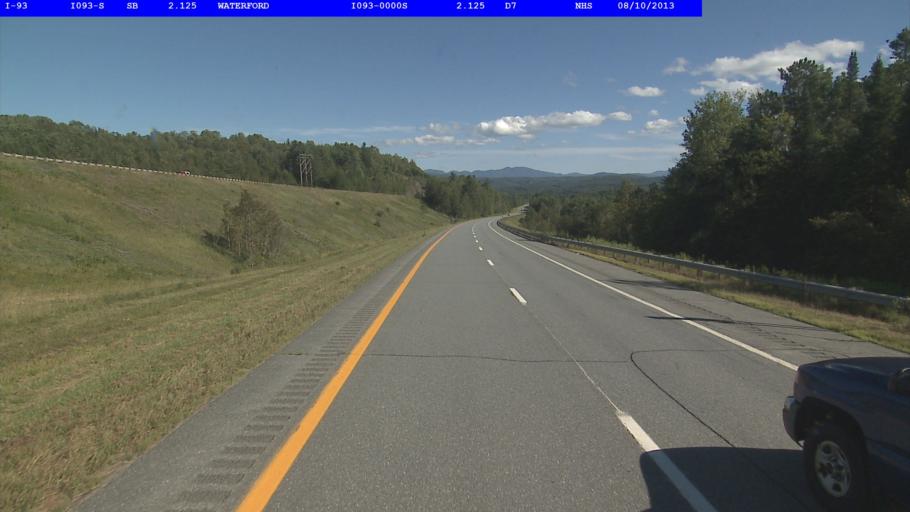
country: US
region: Vermont
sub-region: Caledonia County
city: Saint Johnsbury
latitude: 44.3717
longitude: -71.9070
